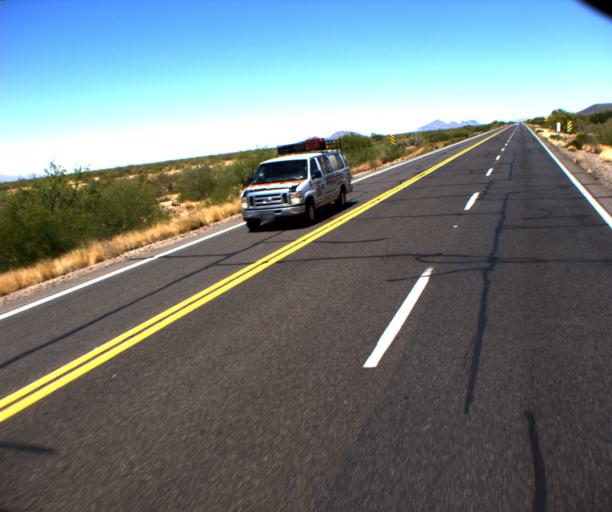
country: US
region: Arizona
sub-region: Yavapai County
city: Congress
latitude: 34.1344
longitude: -112.9663
